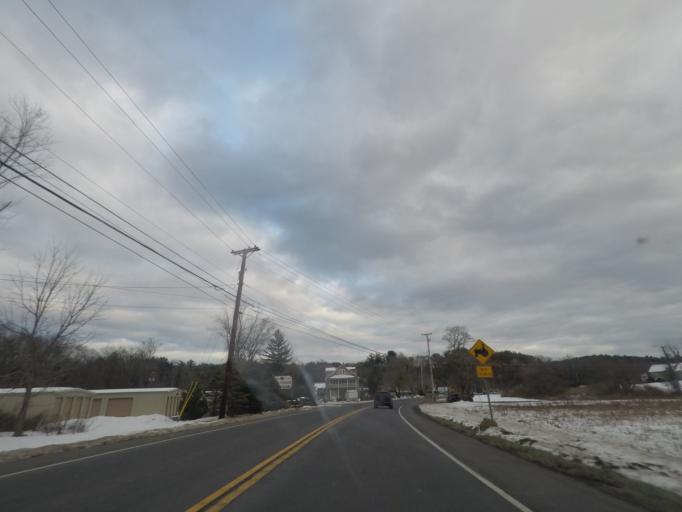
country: US
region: New York
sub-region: Ulster County
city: Tillson
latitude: 41.8195
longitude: -74.0601
